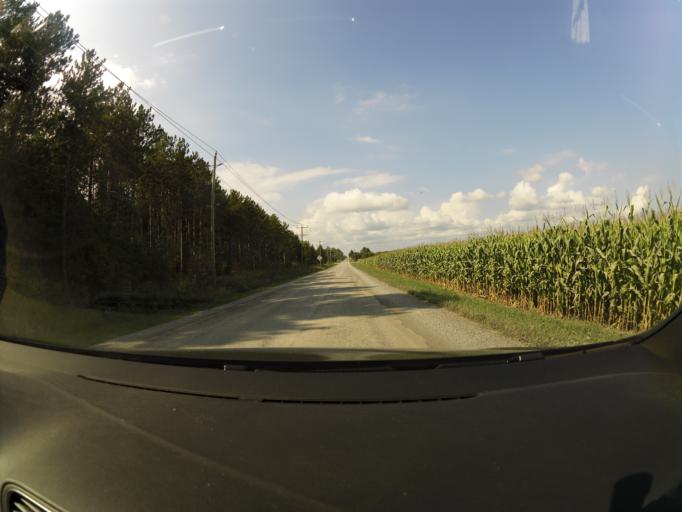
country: CA
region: Ontario
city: Arnprior
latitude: 45.4021
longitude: -76.2263
